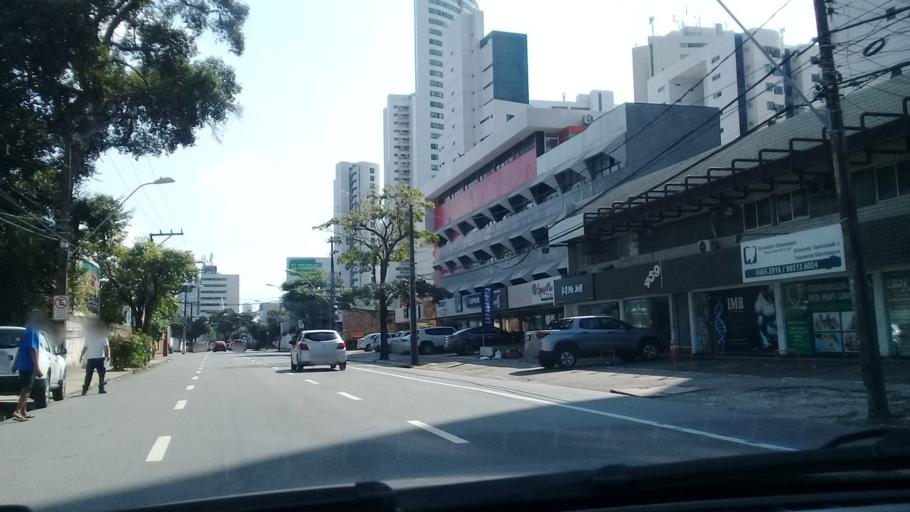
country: BR
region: Pernambuco
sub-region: Recife
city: Recife
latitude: -8.0947
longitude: -34.8844
